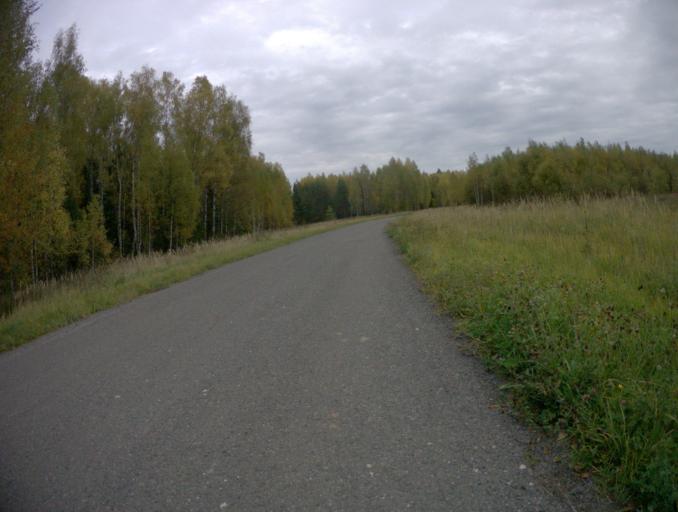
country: RU
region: Vladimir
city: Mstera
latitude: 56.3725
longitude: 41.7748
